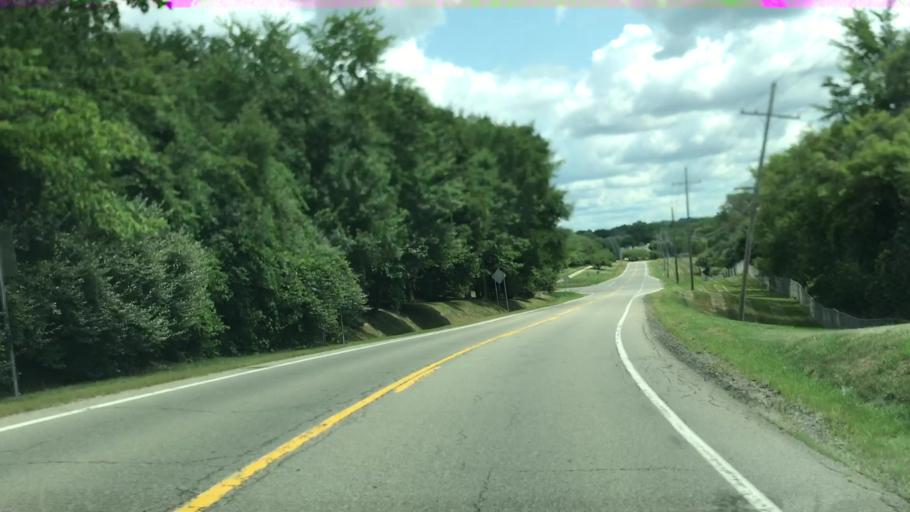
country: US
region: Michigan
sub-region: Oakland County
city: Rochester
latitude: 42.6879
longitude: -83.1170
